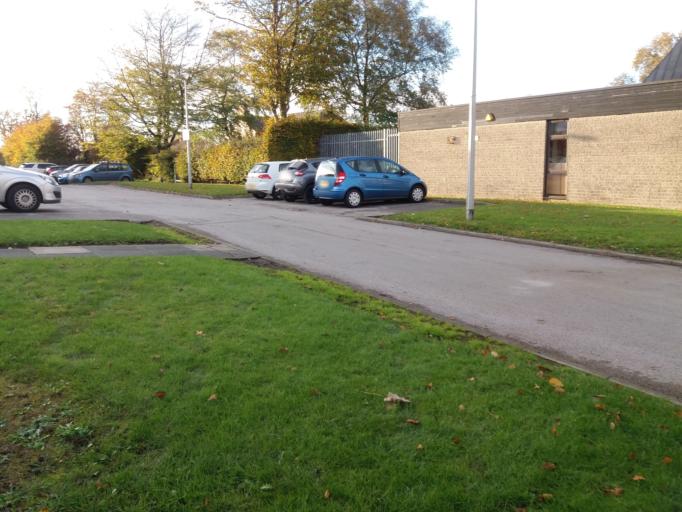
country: GB
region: England
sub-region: Lancashire
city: Coppull
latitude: 53.6210
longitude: -2.6641
